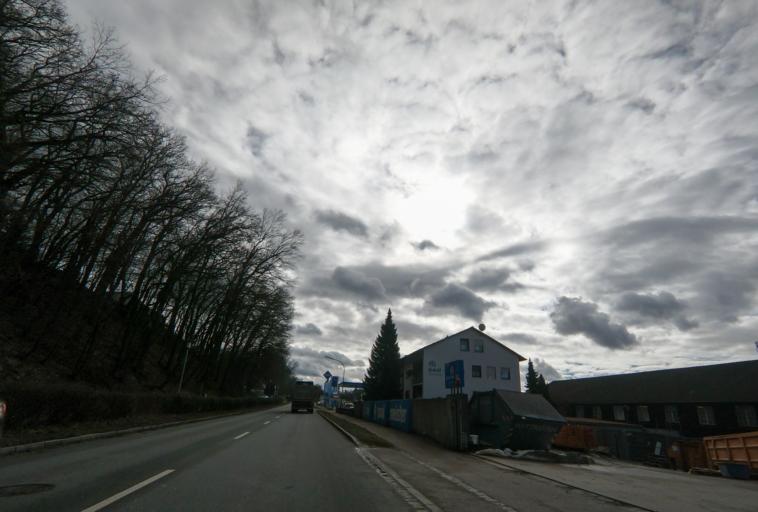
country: DE
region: Bavaria
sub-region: Lower Bavaria
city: Ergoldsbach
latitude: 48.6855
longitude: 12.2062
